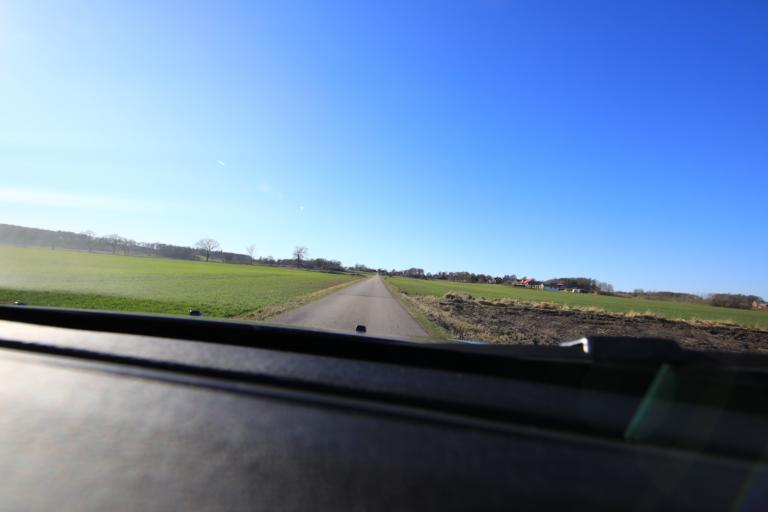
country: SE
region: Halland
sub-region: Varbergs Kommun
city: Tvaaker
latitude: 57.0642
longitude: 12.4051
